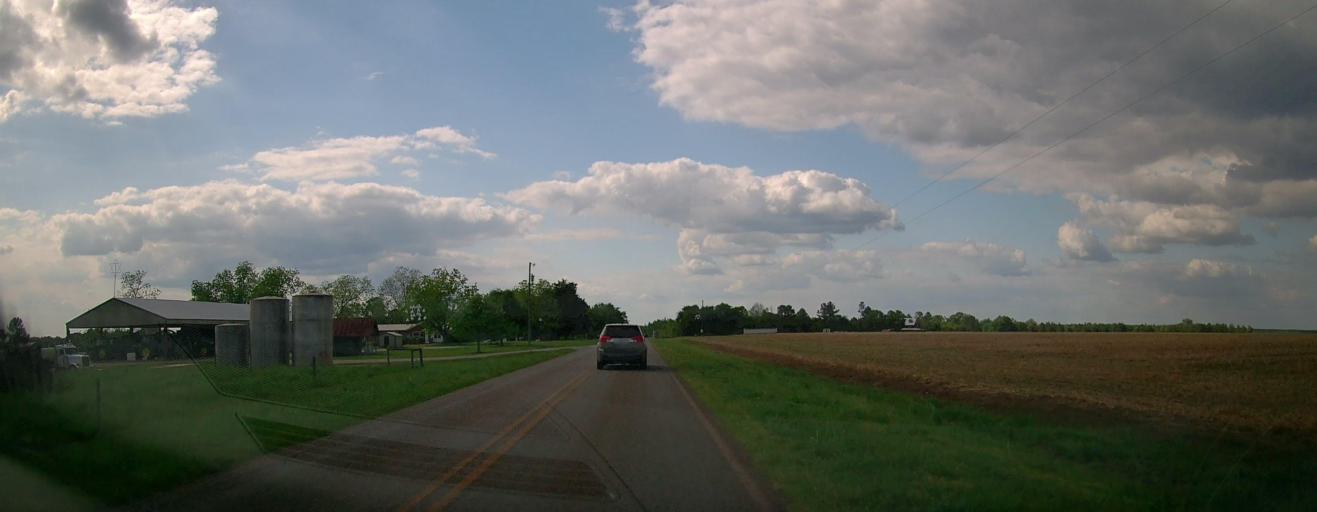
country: US
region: Georgia
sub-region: Laurens County
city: East Dublin
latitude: 32.6857
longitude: -82.8943
